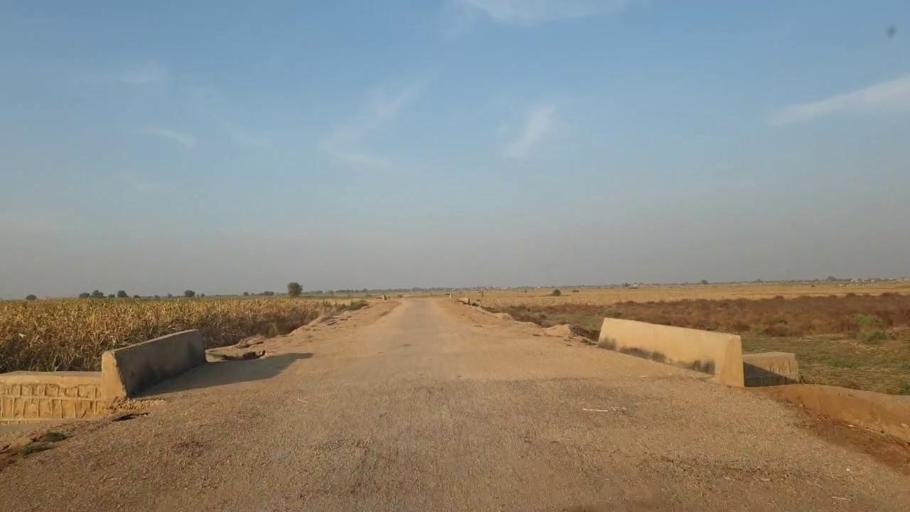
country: PK
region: Sindh
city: Sann
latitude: 25.9217
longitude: 68.1794
